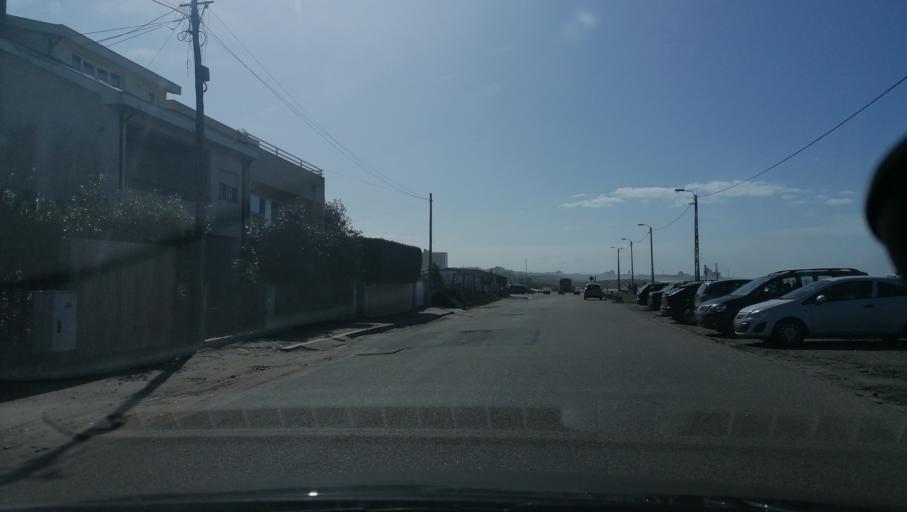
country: PT
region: Porto
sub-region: Vila Nova de Gaia
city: Arcozelo
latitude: 41.0349
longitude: -8.6470
